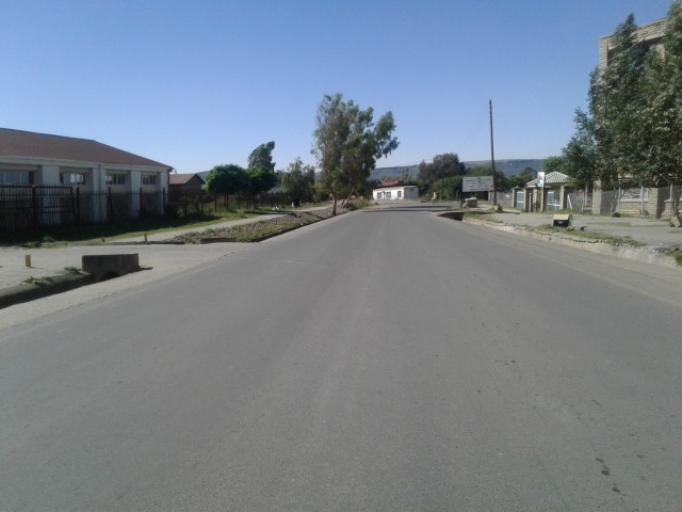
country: LS
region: Maseru
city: Maseru
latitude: -29.3094
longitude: 27.4853
